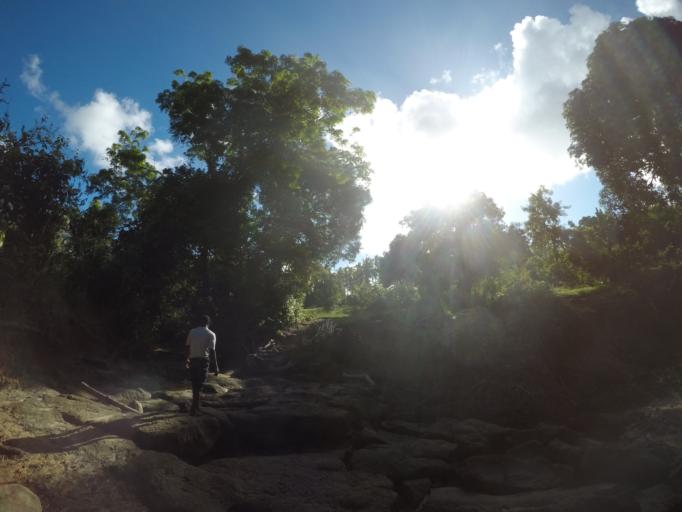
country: TZ
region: Pemba South
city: Mtambile
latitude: -5.3479
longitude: 39.6974
